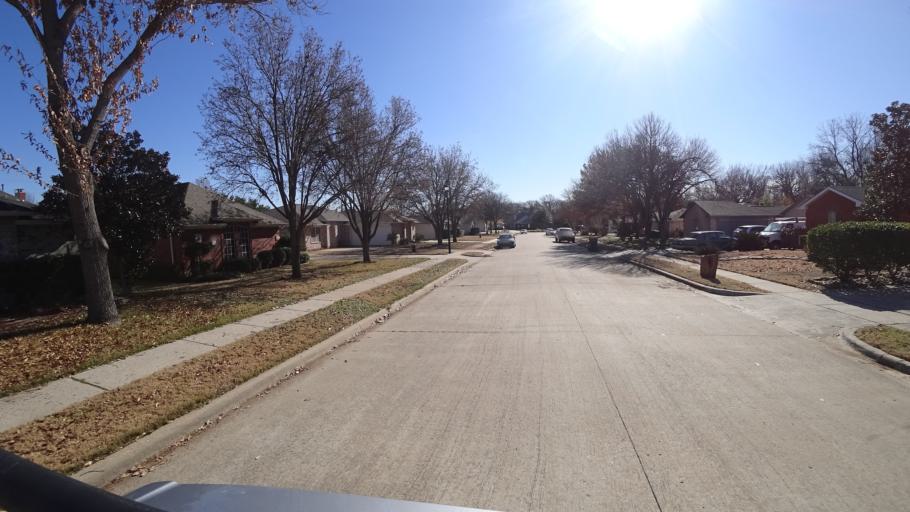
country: US
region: Texas
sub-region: Denton County
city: Lewisville
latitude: 33.0172
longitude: -97.0078
